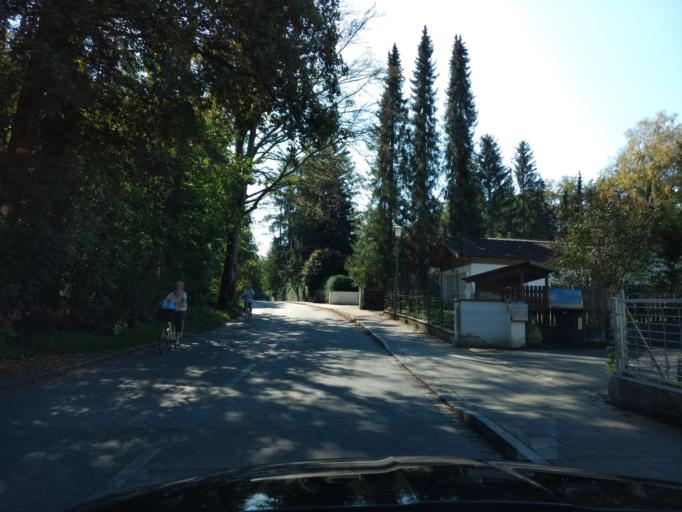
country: DE
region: Bavaria
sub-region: Upper Bavaria
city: Geretsried
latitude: 47.8790
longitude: 11.4760
